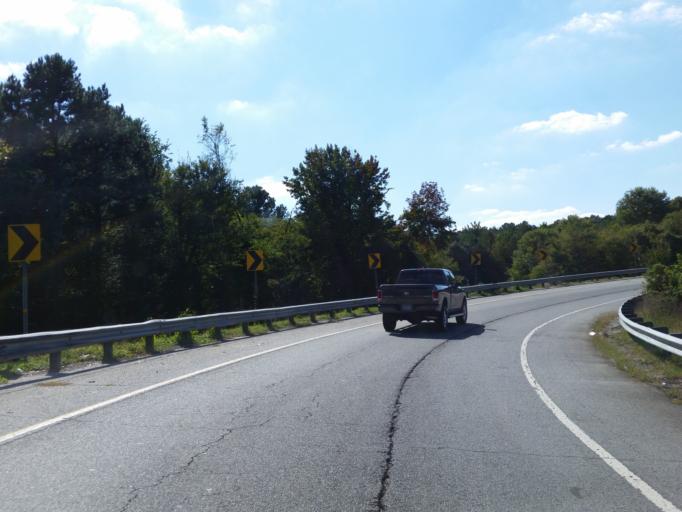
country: US
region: Georgia
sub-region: Fulton County
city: Hapeville
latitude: 33.6311
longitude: -84.4017
